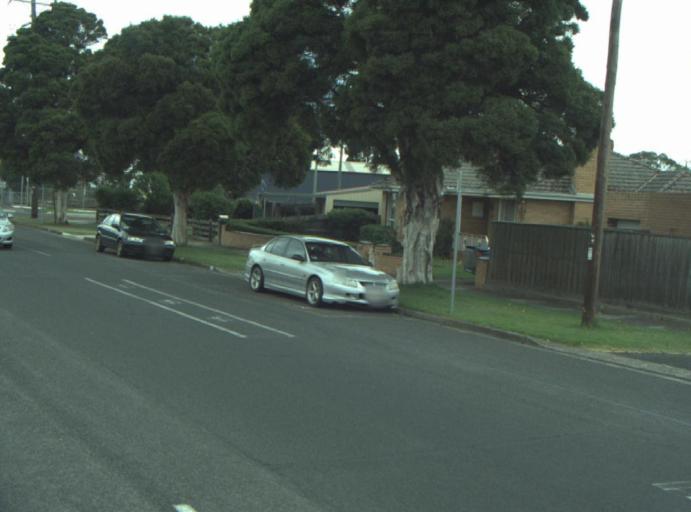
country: AU
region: Victoria
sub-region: Greater Geelong
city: East Geelong
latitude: -38.1603
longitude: 144.3633
